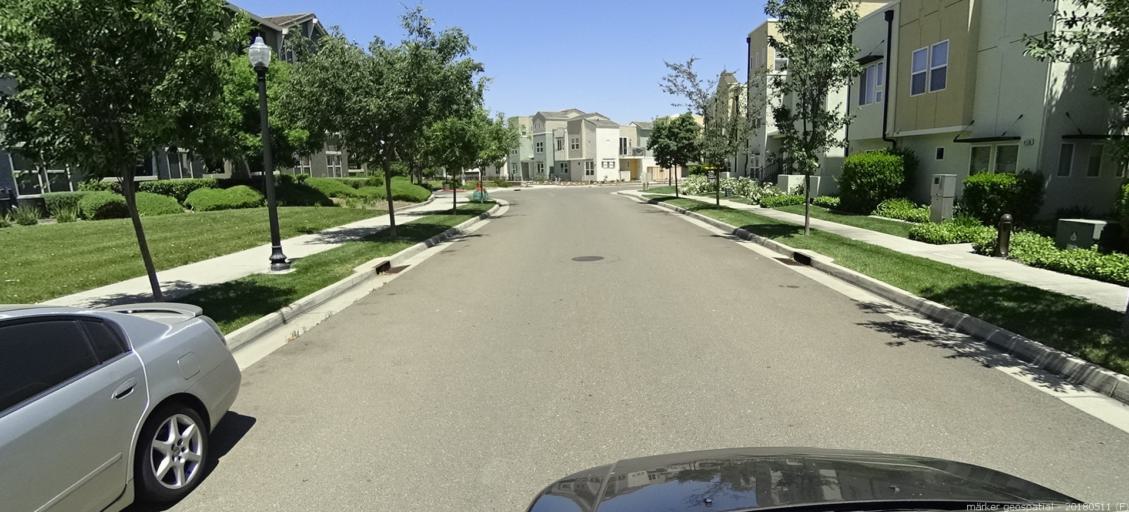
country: US
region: California
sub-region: Yolo County
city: West Sacramento
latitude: 38.6423
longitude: -121.5158
